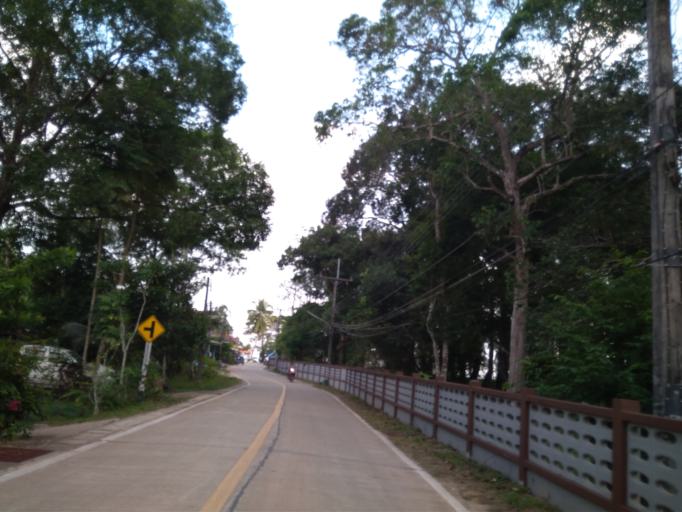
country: TH
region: Phangnga
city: Ko Yao
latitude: 8.1361
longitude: 98.6255
